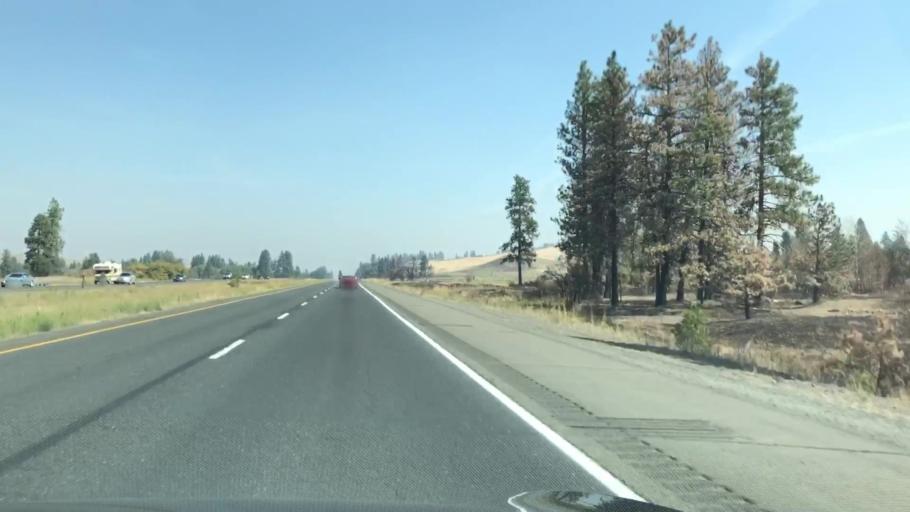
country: US
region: Washington
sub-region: Spokane County
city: Medical Lake
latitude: 47.5383
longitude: -117.6437
